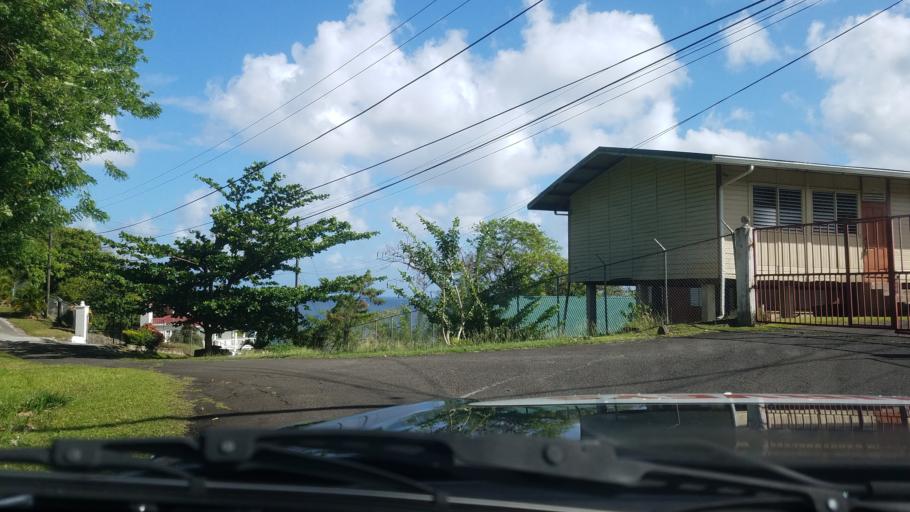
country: LC
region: Castries Quarter
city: Bisee
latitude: 14.0233
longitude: -60.9999
